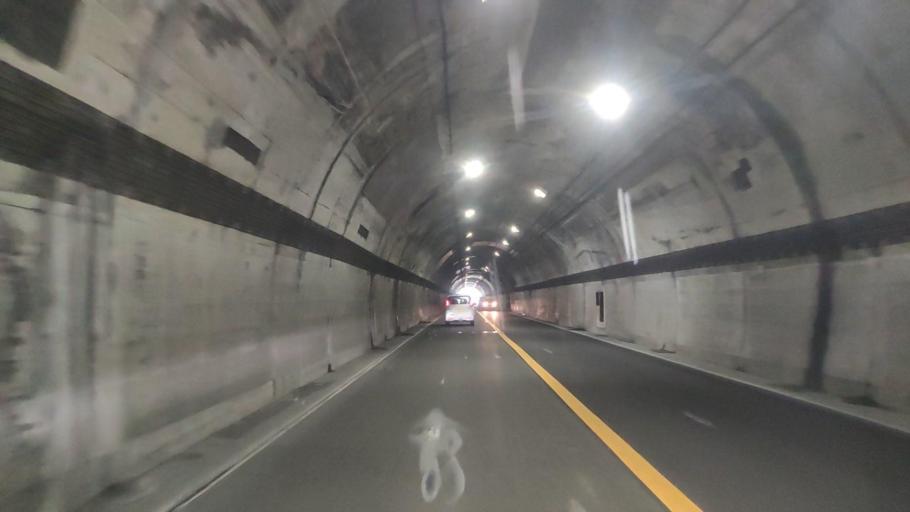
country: JP
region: Wakayama
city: Shingu
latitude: 33.5753
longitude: 135.9180
